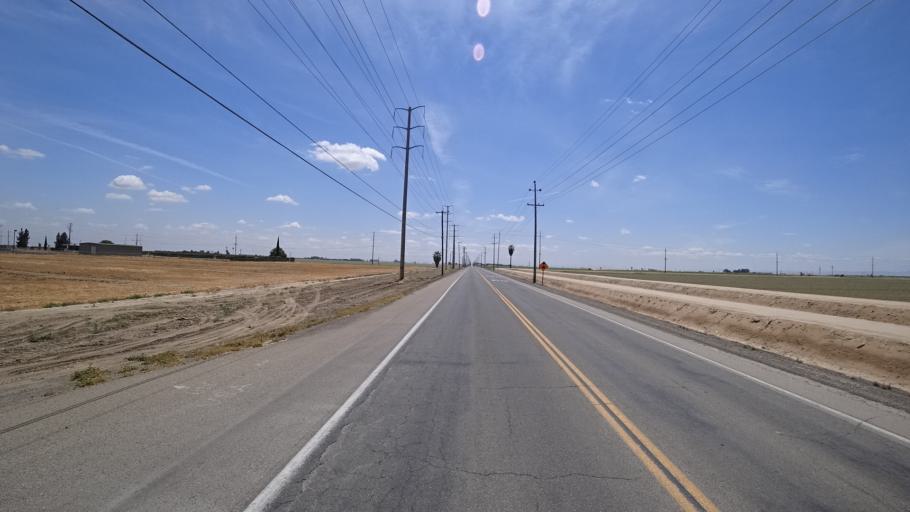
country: US
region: California
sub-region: Kings County
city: Home Garden
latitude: 36.2568
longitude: -119.6549
